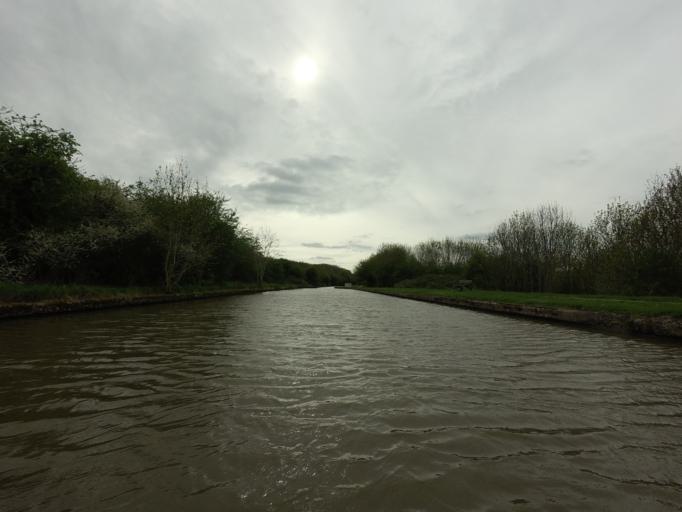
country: GB
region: England
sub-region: Milton Keynes
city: Bradwell
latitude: 52.0607
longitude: -0.7948
